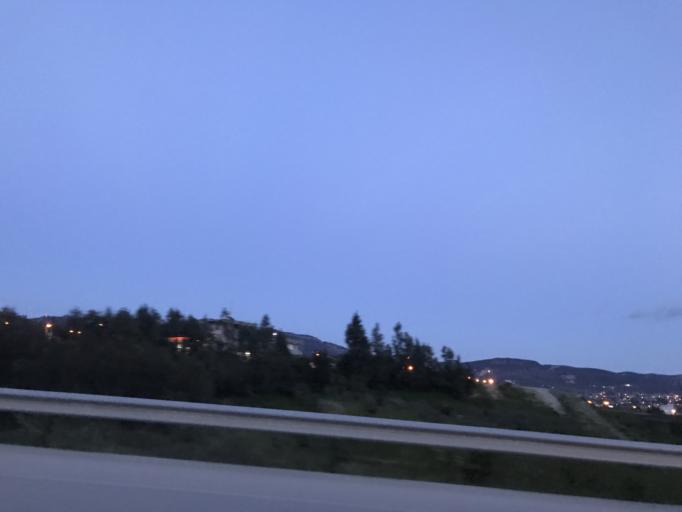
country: TR
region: Hatay
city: Asagiokcular
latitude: 36.1814
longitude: 36.1181
